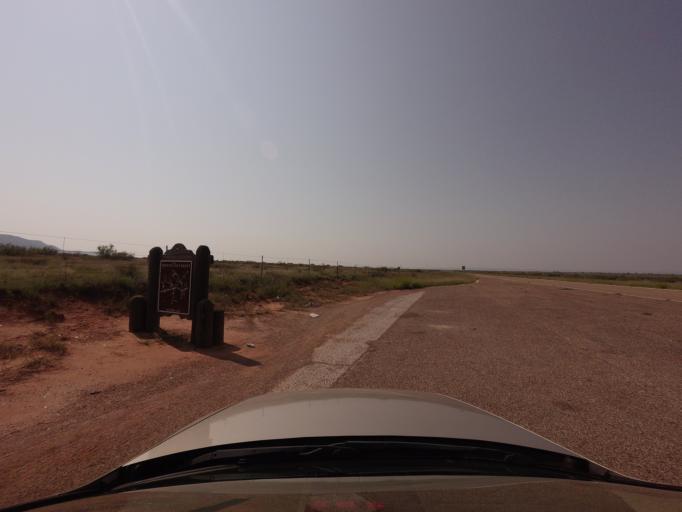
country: US
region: New Mexico
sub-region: Quay County
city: Tucumcari
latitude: 34.9903
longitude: -103.7469
